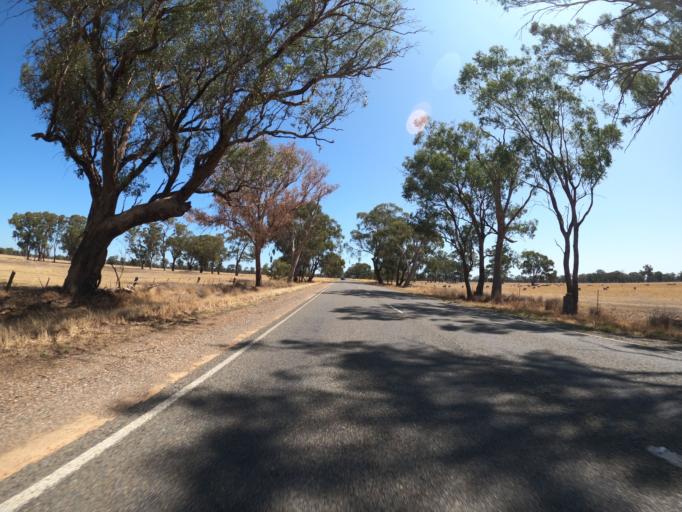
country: AU
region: New South Wales
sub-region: Corowa Shire
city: Corowa
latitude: -36.0711
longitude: 146.3550
